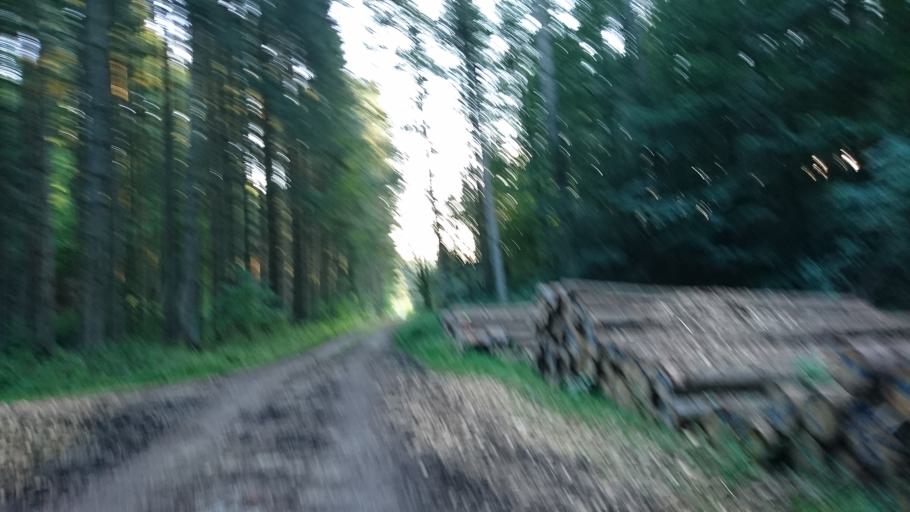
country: DE
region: Bavaria
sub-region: Swabia
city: Zusmarshausen
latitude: 48.4321
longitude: 10.6210
